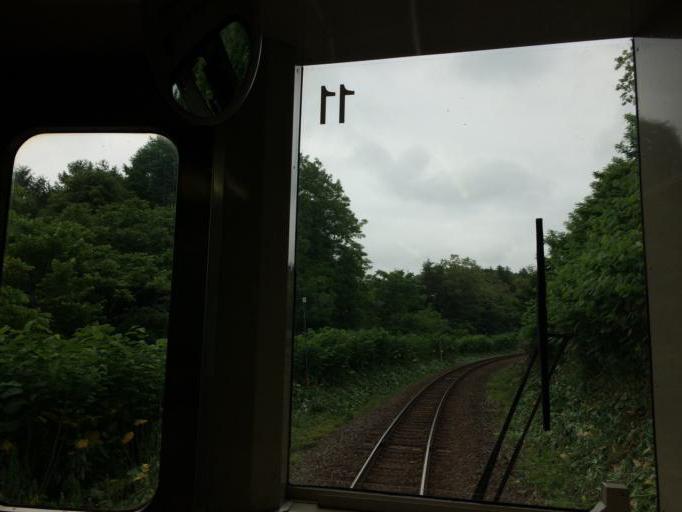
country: JP
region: Hokkaido
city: Iwanai
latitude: 42.9793
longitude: 140.6694
